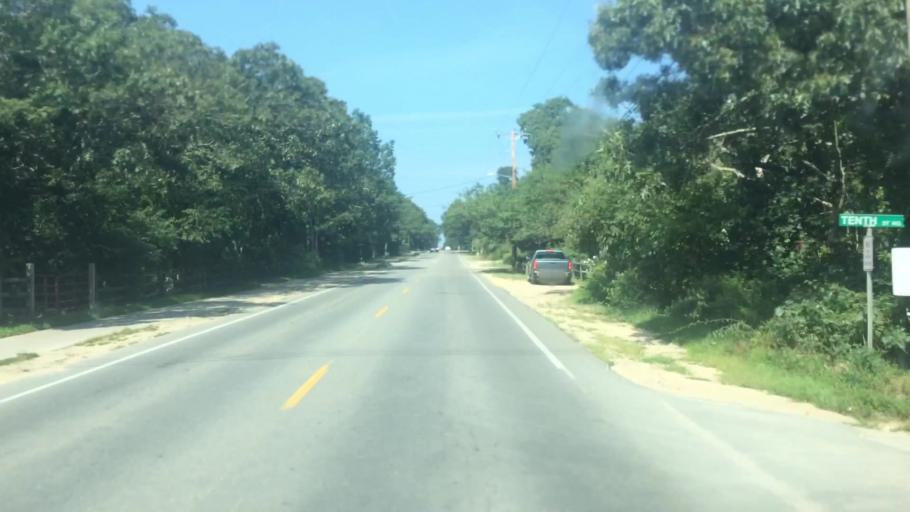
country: US
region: Massachusetts
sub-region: Dukes County
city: Edgartown
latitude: 41.4032
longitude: -70.5559
